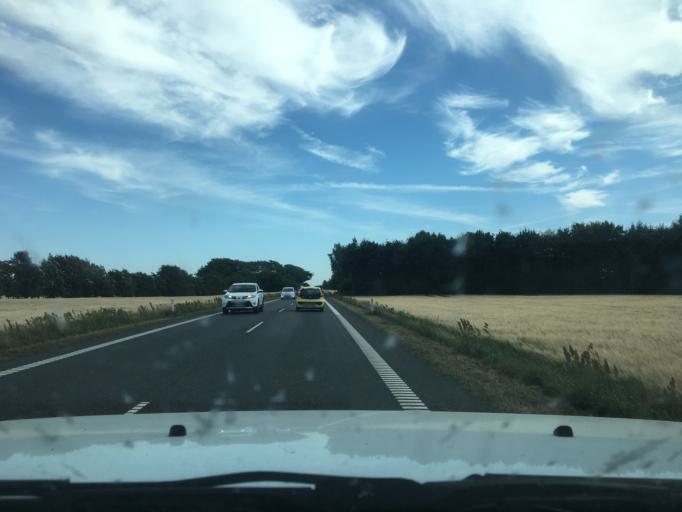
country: DK
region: Central Jutland
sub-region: Viborg Kommune
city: Viborg
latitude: 56.5919
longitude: 9.3656
